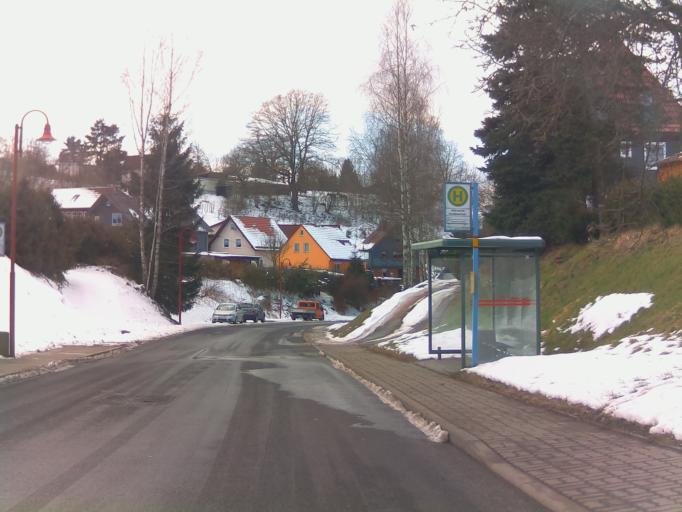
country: DE
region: Thuringia
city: Zella-Mehlis
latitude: 50.6162
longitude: 10.6472
